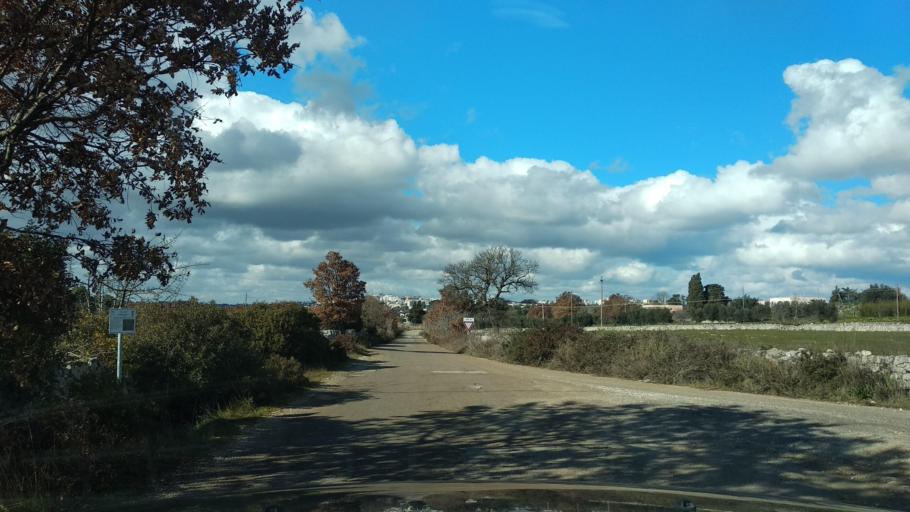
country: IT
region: Apulia
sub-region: Provincia di Brindisi
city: Casalini
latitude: 40.7218
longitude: 17.4468
